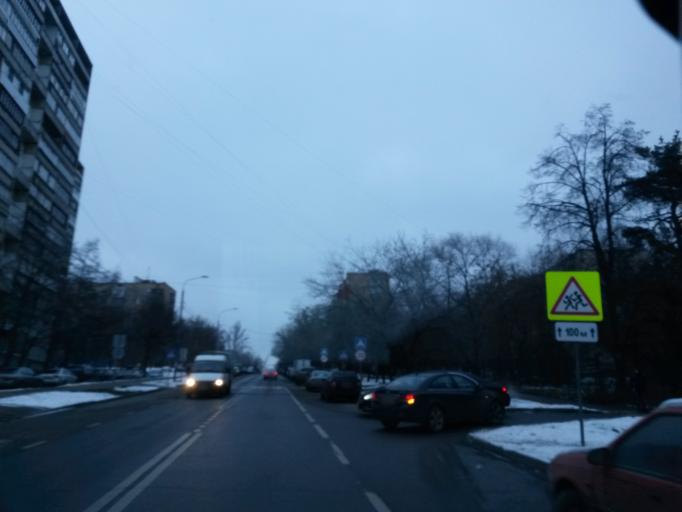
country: RU
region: Moskovskaya
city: Bol'shaya Setun'
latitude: 55.7169
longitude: 37.4374
